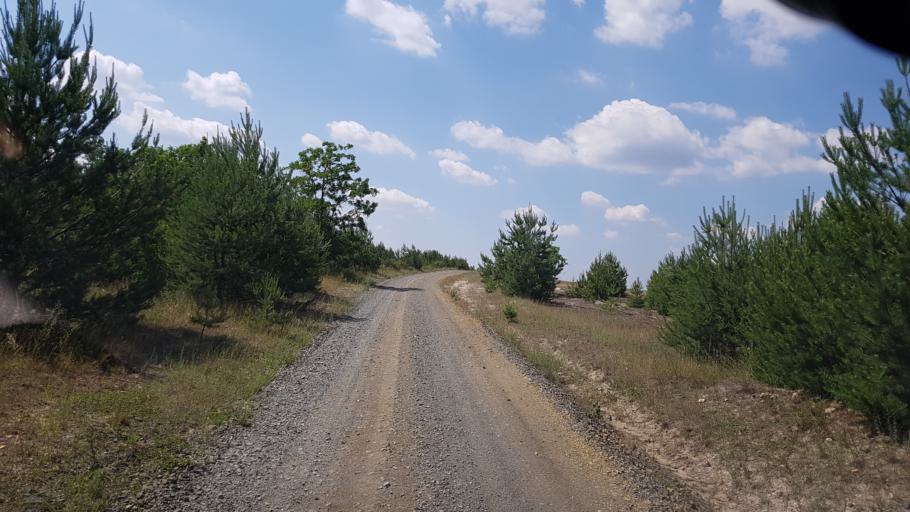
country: DE
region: Brandenburg
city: Sallgast
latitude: 51.5632
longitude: 13.8028
